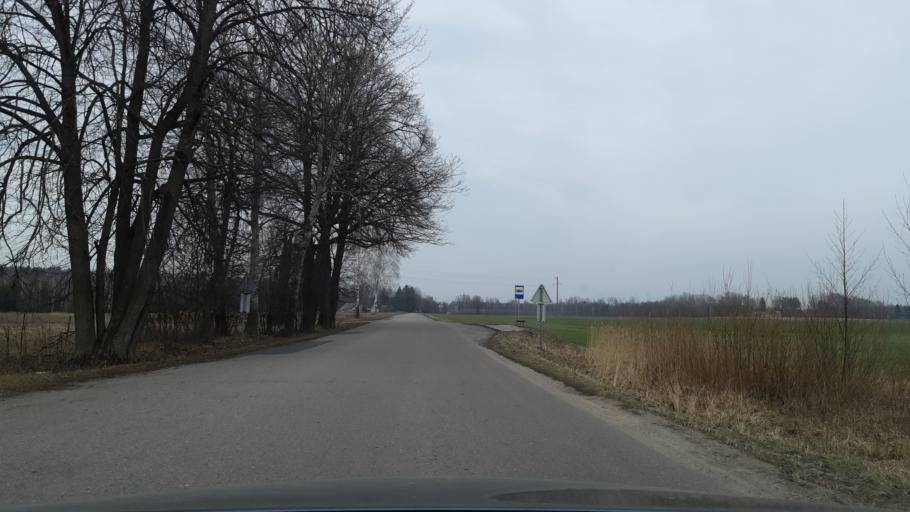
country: LT
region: Marijampoles apskritis
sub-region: Marijampole Municipality
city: Marijampole
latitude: 54.7276
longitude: 23.3363
